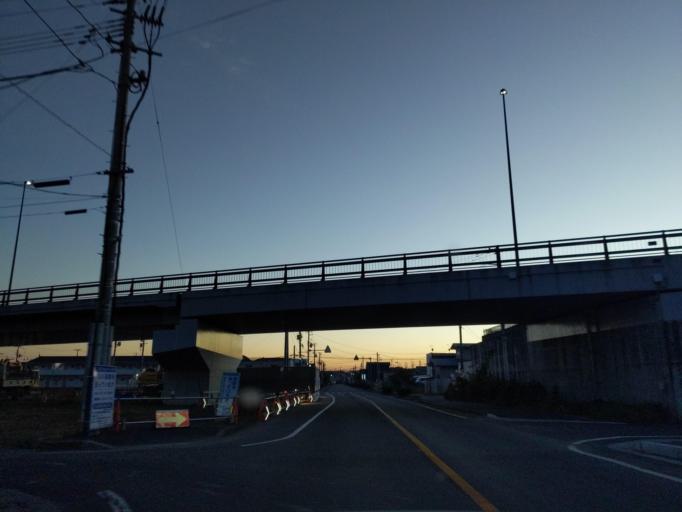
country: JP
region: Fukushima
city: Koriyama
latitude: 37.3581
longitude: 140.3768
